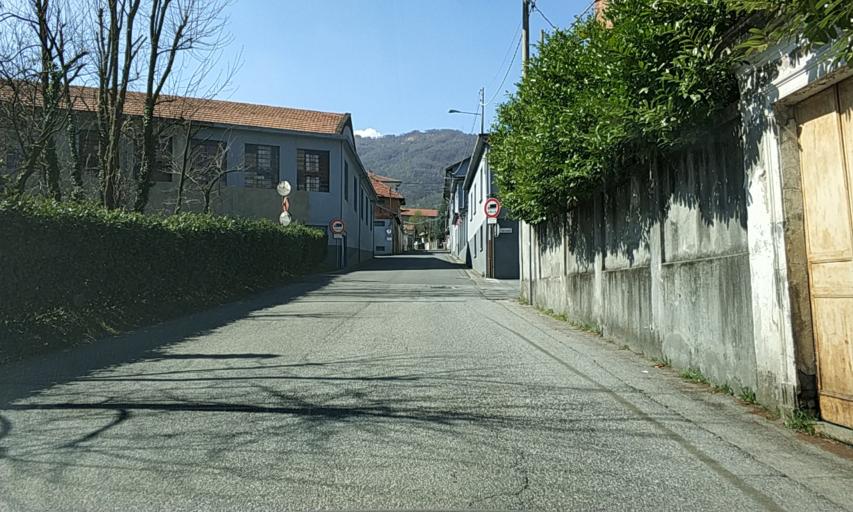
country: IT
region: Piedmont
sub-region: Provincia di Torino
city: Forno Canavese
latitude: 45.3435
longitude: 7.5912
